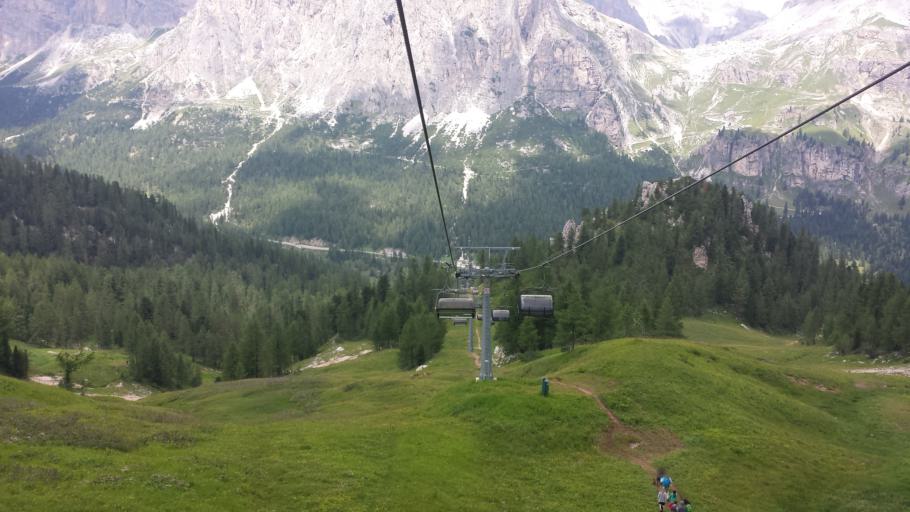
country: IT
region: Veneto
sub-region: Provincia di Belluno
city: Selva di Cadore
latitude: 46.5098
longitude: 12.0453
